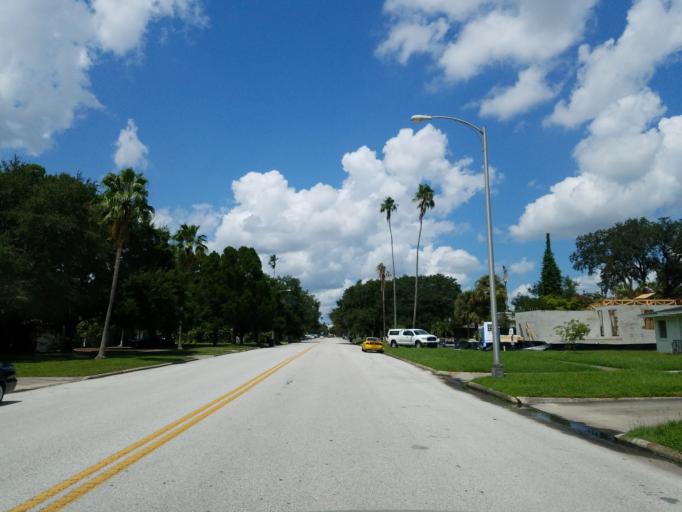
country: US
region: Florida
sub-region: Hillsborough County
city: Tampa
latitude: 27.9221
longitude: -82.4509
